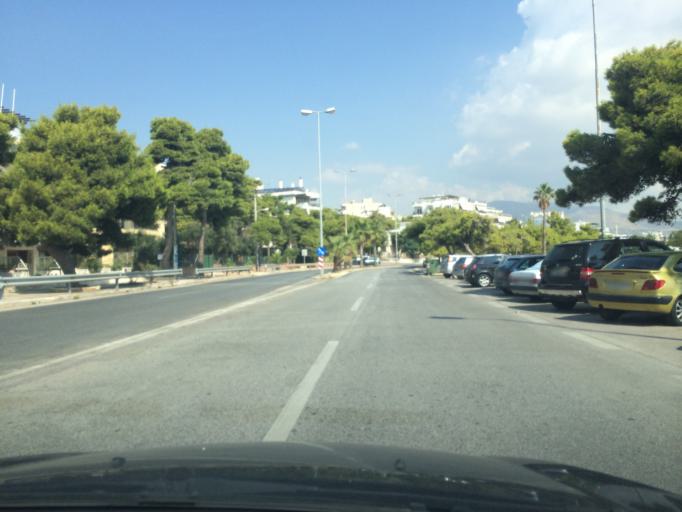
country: GR
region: Attica
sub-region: Nomarchia Anatolikis Attikis
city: Vari
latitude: 37.8141
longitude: 23.8009
